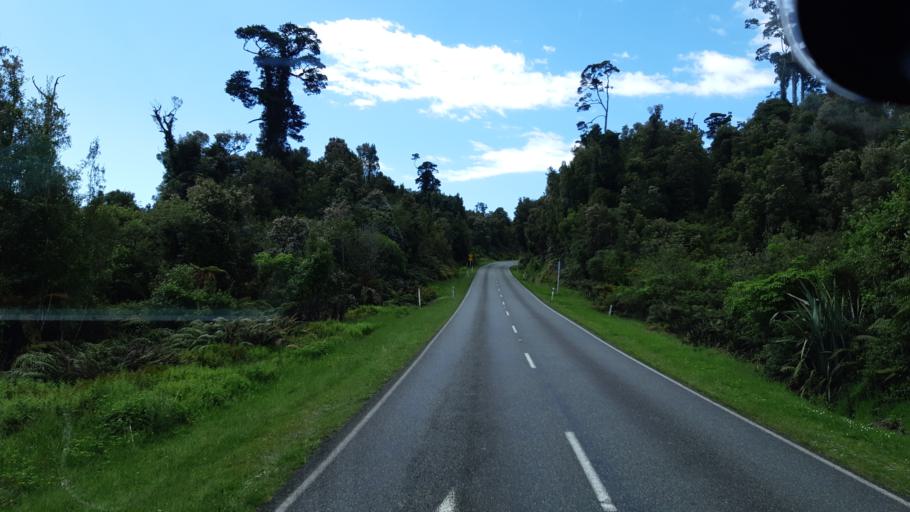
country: NZ
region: West Coast
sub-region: Westland District
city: Hokitika
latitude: -43.0494
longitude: 170.6379
